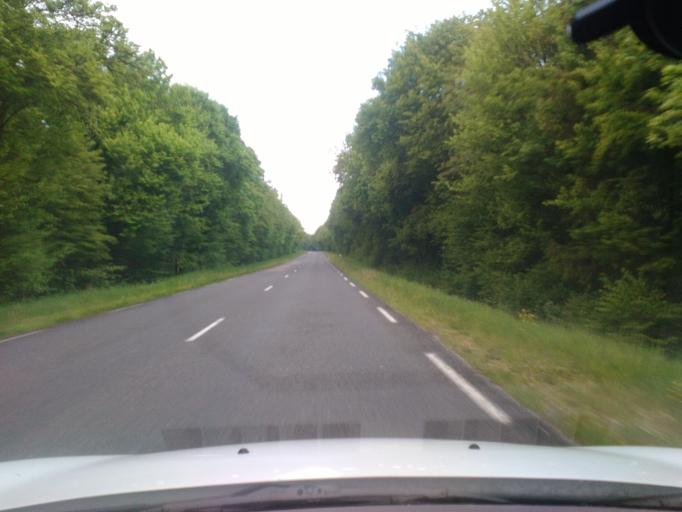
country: FR
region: Champagne-Ardenne
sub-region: Departement de la Haute-Marne
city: Lavilleneuve-au-Roi
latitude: 48.2120
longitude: 4.9204
